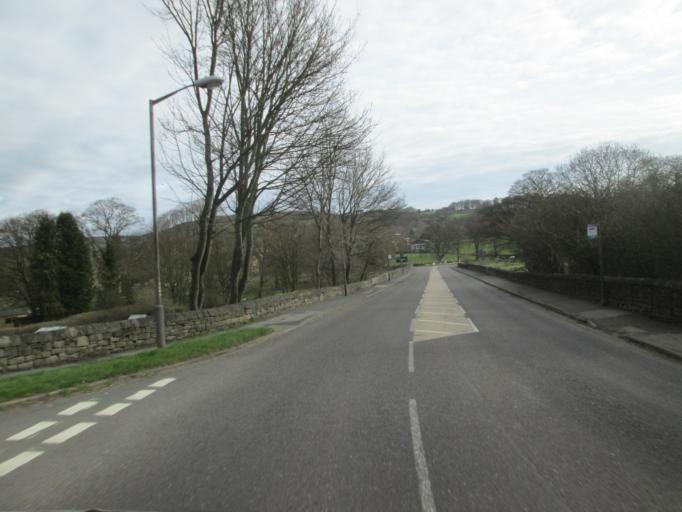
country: GB
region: England
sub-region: Derbyshire
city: Bakewell
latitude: 53.2456
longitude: -1.6243
